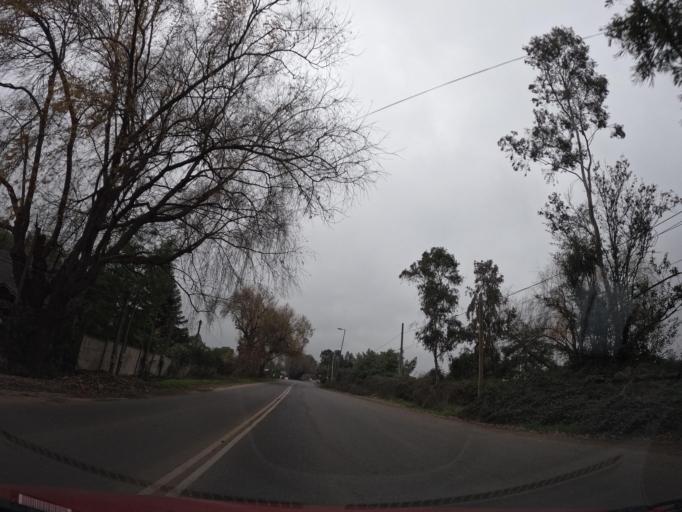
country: CL
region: Maule
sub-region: Provincia de Talca
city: San Clemente
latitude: -35.5515
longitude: -71.4704
